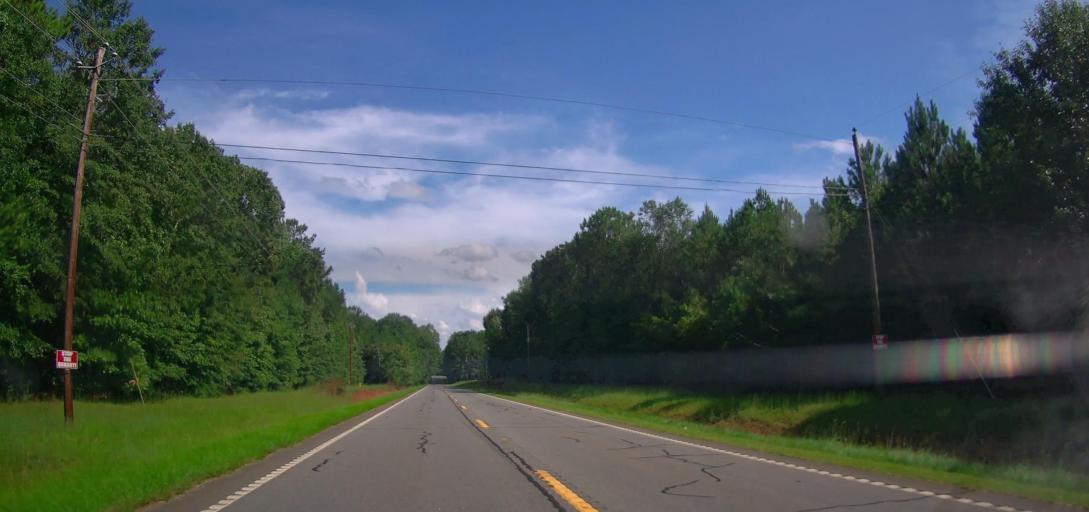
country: US
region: Georgia
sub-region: Talbot County
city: Sardis
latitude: 32.8217
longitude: -84.6112
